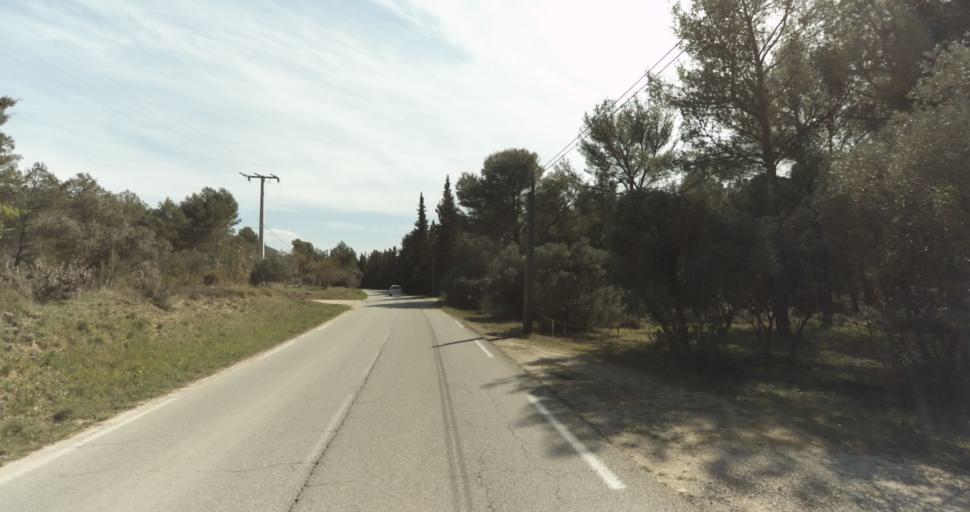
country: FR
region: Provence-Alpes-Cote d'Azur
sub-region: Departement des Bouches-du-Rhone
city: Ventabren
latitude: 43.5286
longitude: 5.2856
